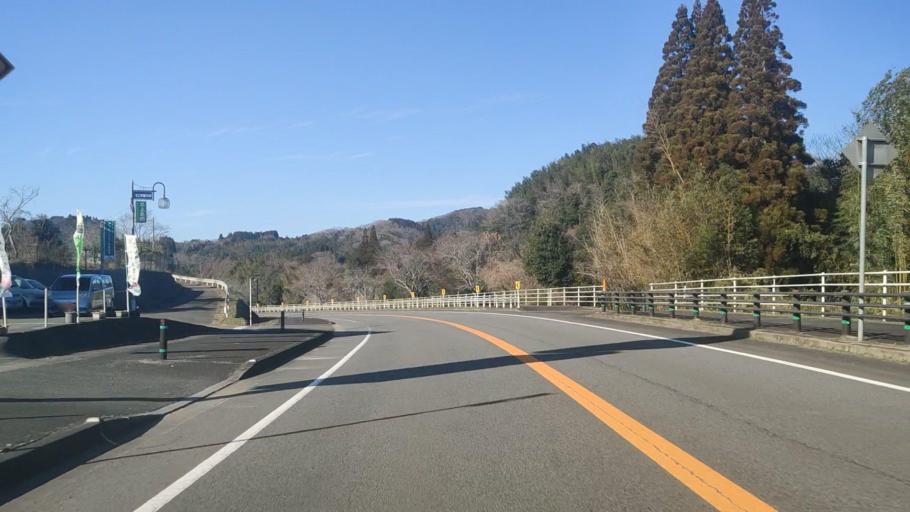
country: JP
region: Oita
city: Usuki
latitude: 33.0593
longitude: 131.6732
